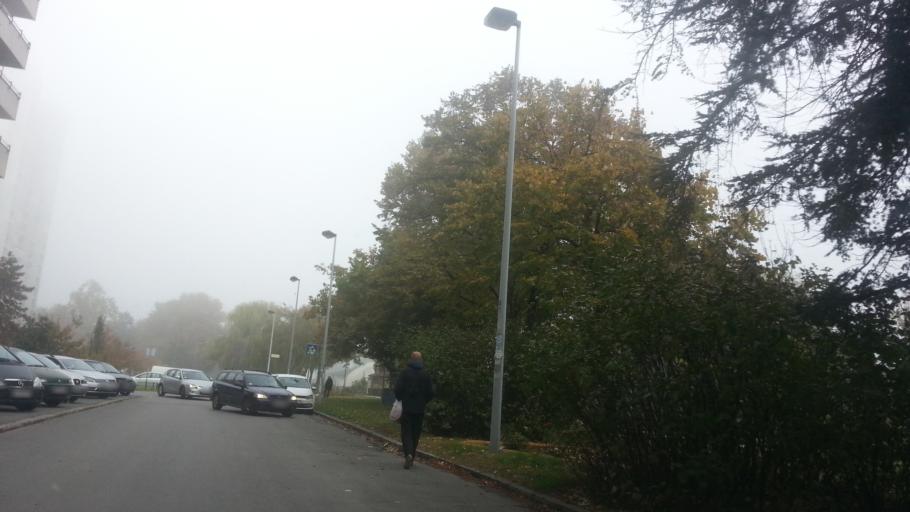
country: RS
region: Central Serbia
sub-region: Belgrade
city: Zemun
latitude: 44.8384
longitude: 20.4186
